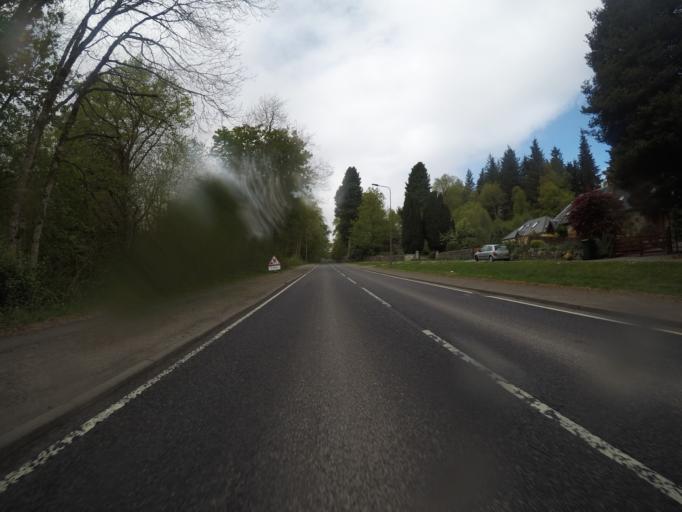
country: GB
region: Scotland
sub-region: Highland
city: Spean Bridge
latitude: 57.0692
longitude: -4.7968
